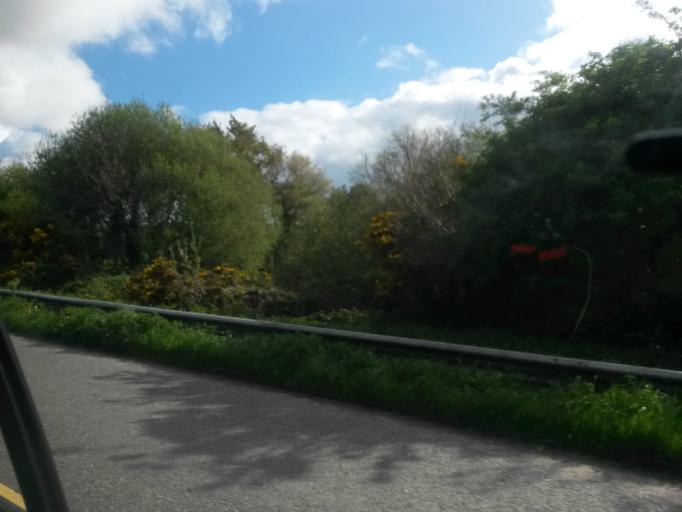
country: IE
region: Leinster
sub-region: Loch Garman
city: Enniscorthy
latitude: 52.5173
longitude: -6.5651
